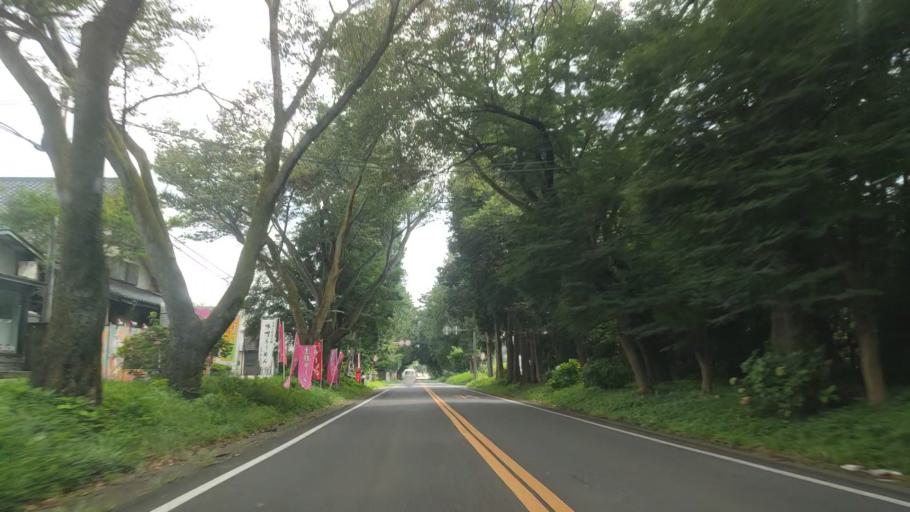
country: JP
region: Tochigi
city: Utsunomiya-shi
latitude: 36.6216
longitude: 139.8532
